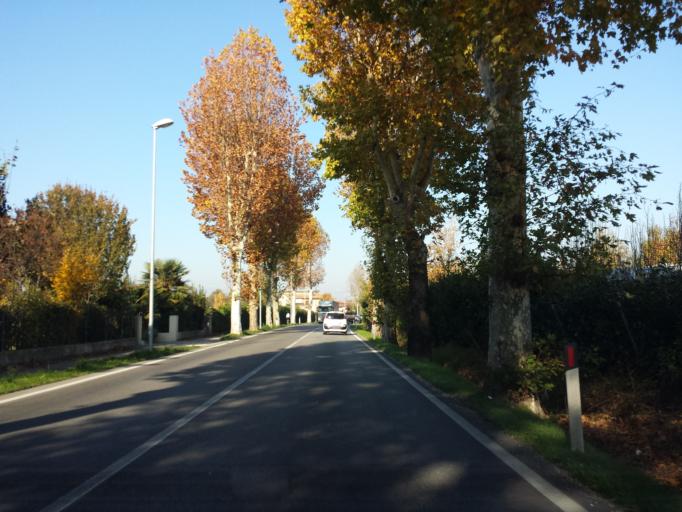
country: IT
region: Veneto
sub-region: Provincia di Treviso
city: Valla
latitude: 45.6976
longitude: 11.9284
